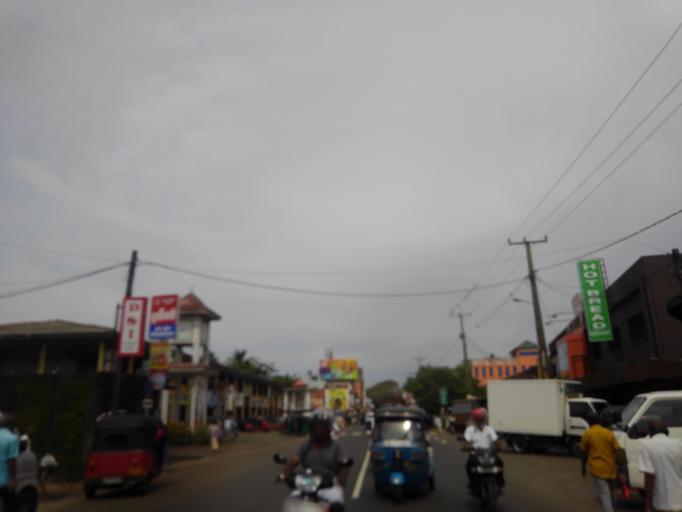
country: LK
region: Western
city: Beruwala
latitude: 6.4751
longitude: 79.9836
